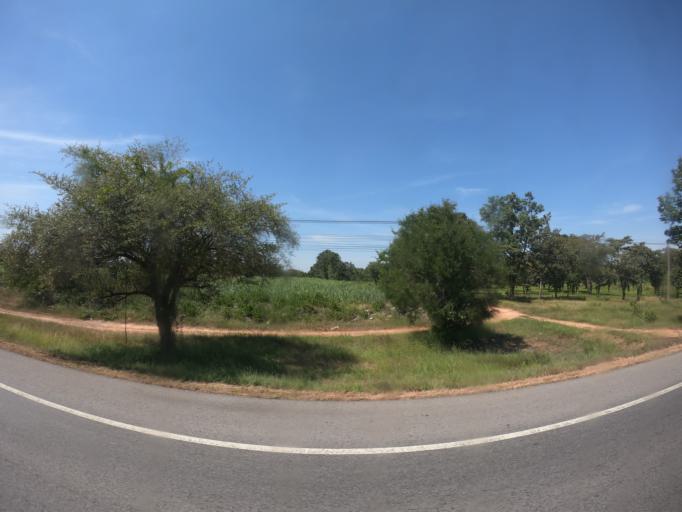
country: TH
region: Khon Kaen
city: Phon
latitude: 15.7357
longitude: 102.5972
